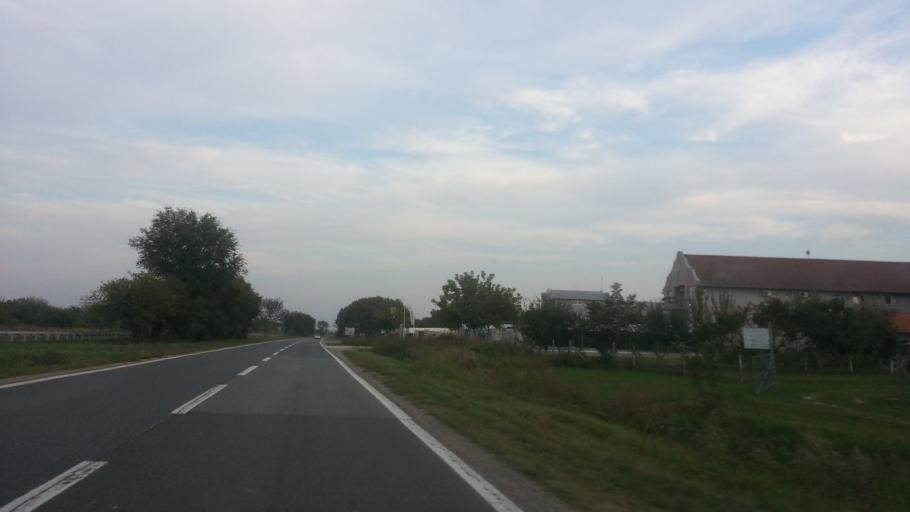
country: RS
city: Novi Banovci
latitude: 44.8794
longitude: 20.3210
